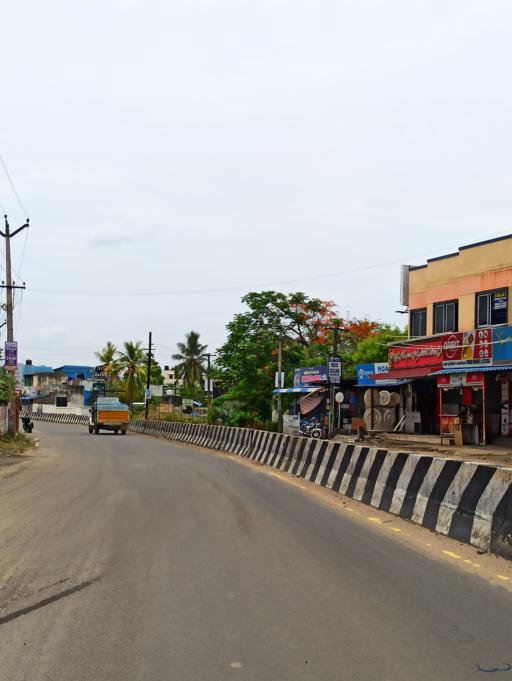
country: IN
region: Tamil Nadu
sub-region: Kancheepuram
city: Vandalur
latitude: 12.9092
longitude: 80.0689
